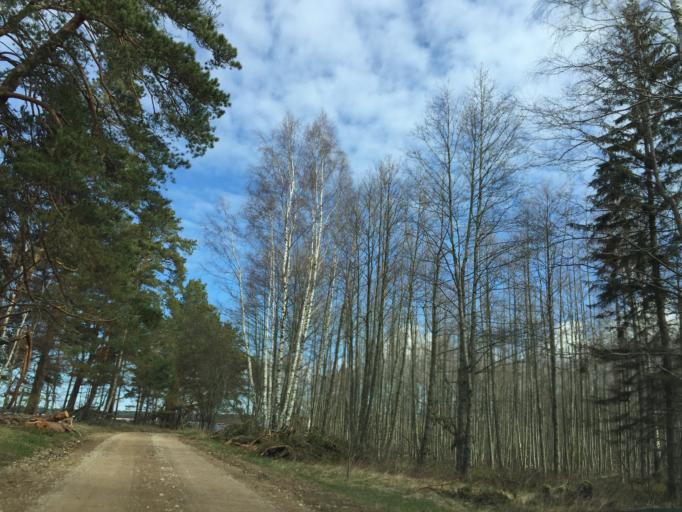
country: LV
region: Salacgrivas
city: Salacgriva
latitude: 57.6024
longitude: 24.3759
